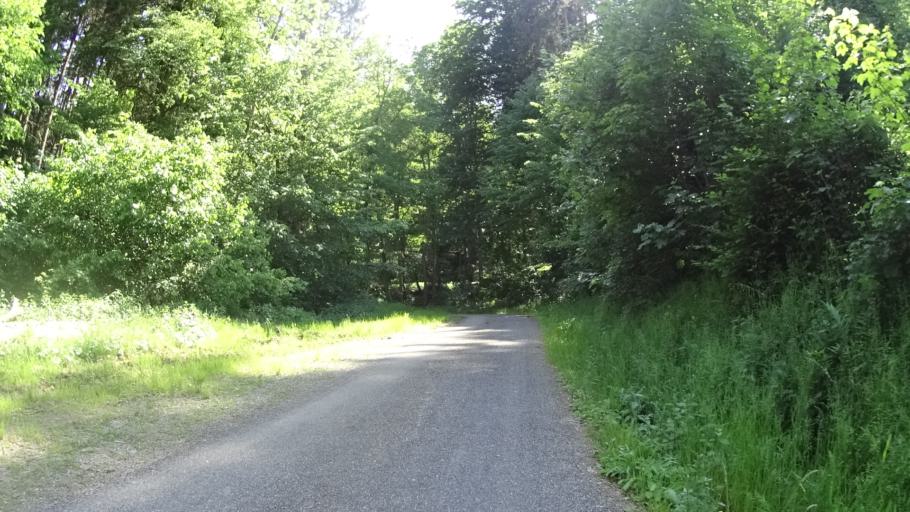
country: DE
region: Baden-Wuerttemberg
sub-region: Karlsruhe Region
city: Hopfingen
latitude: 49.6319
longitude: 9.4402
